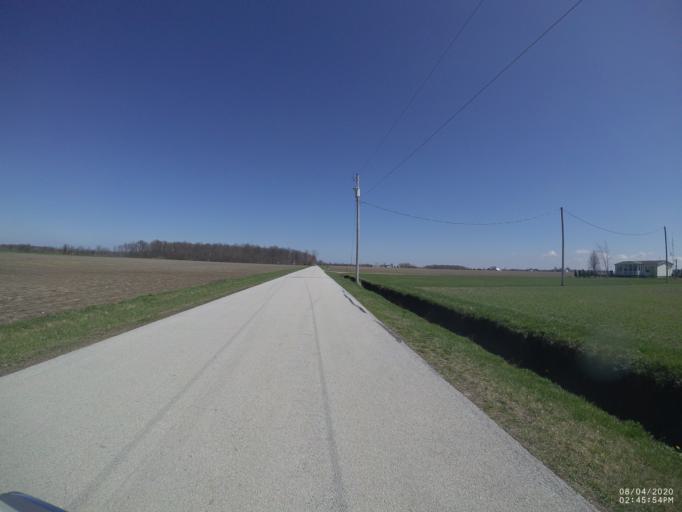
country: US
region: Ohio
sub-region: Sandusky County
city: Gibsonburg
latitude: 41.2974
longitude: -83.2868
